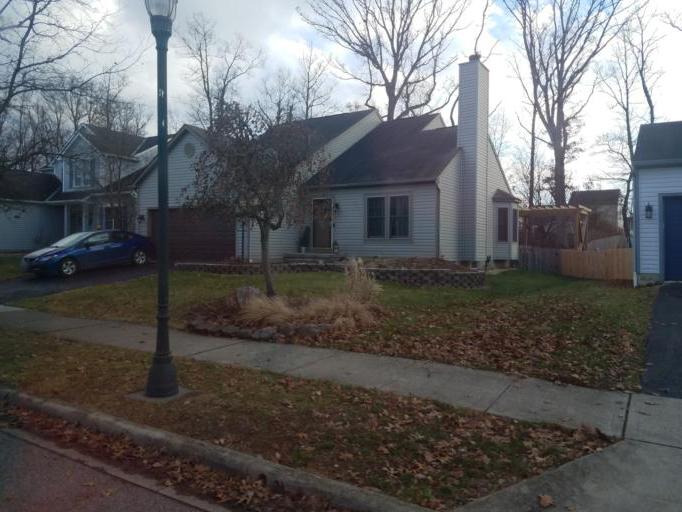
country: US
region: Ohio
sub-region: Delaware County
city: Delaware
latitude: 40.3169
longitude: -83.1069
